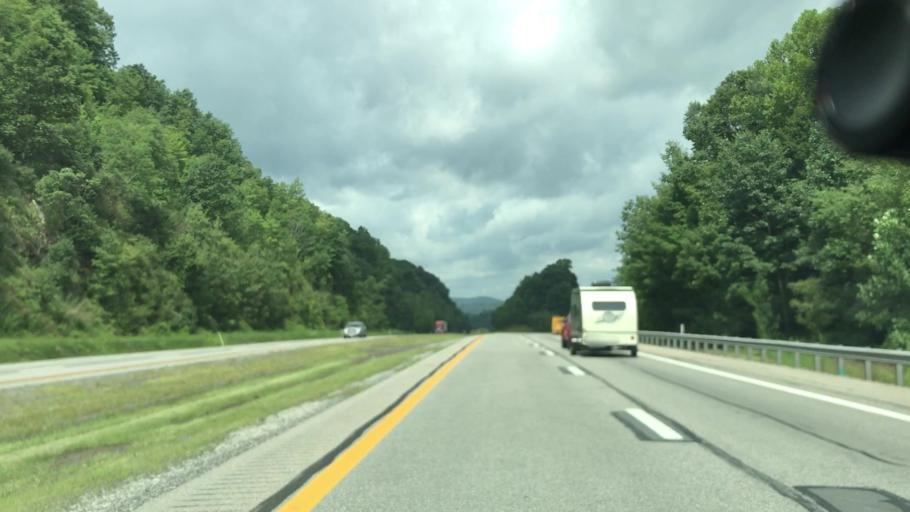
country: US
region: West Virginia
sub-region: Fayette County
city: Oak Hill
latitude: 37.9665
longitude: -81.2725
